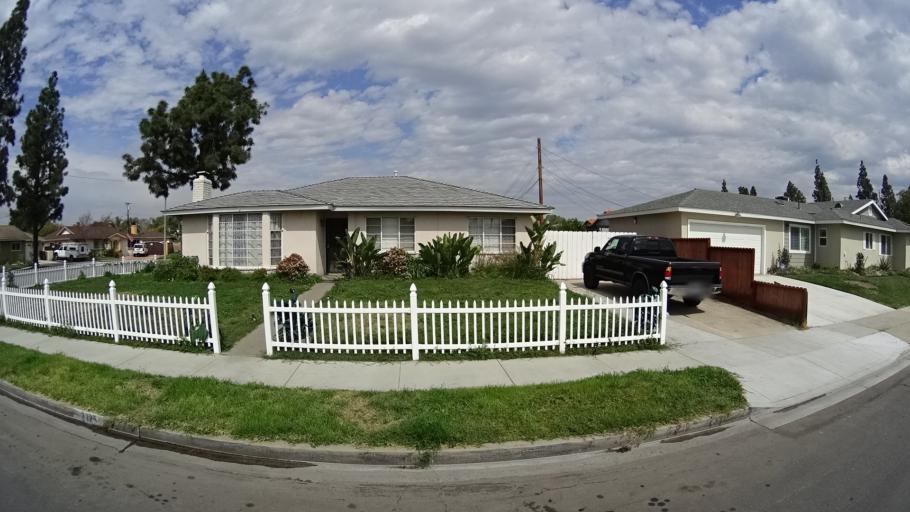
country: US
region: California
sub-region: Orange County
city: Anaheim
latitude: 33.8349
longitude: -117.8837
